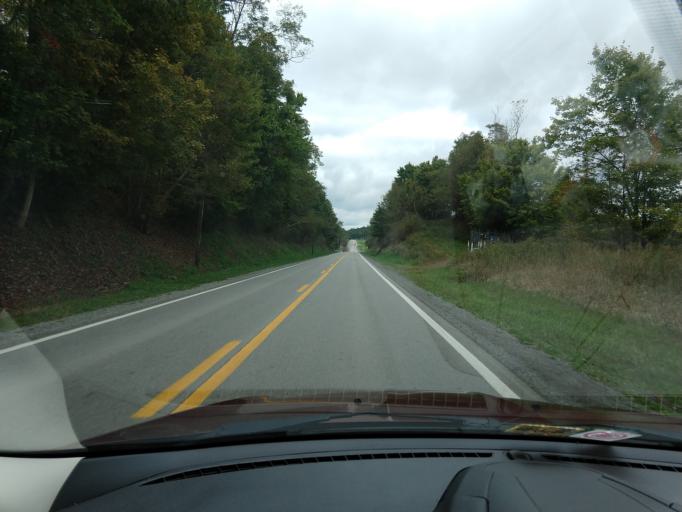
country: US
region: West Virginia
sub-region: Barbour County
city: Philippi
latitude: 39.1035
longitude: -79.9950
